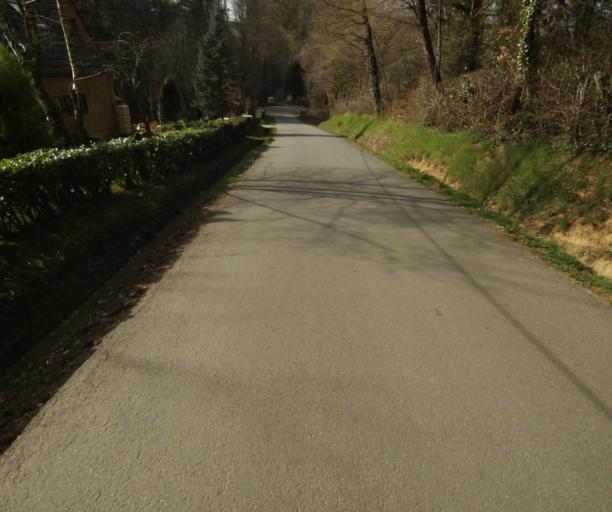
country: FR
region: Limousin
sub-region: Departement de la Correze
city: Naves
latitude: 45.3122
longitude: 1.7261
